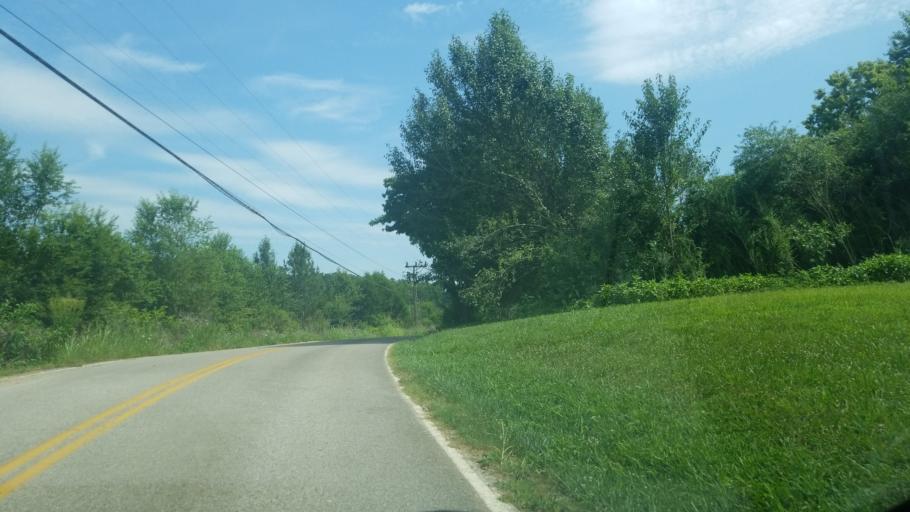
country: US
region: Tennessee
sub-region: Hamilton County
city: Lakesite
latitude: 35.2341
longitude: -85.0143
